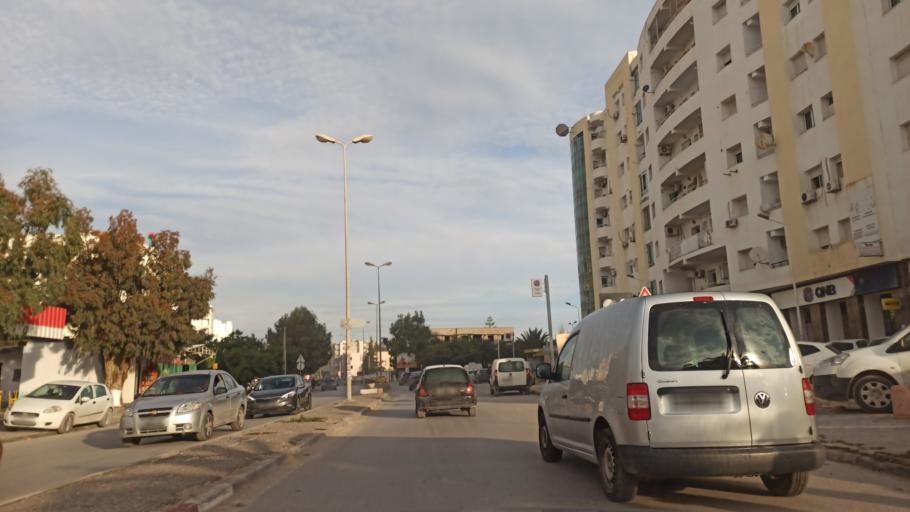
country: TN
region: Ariana
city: Ariana
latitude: 36.8589
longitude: 10.2561
